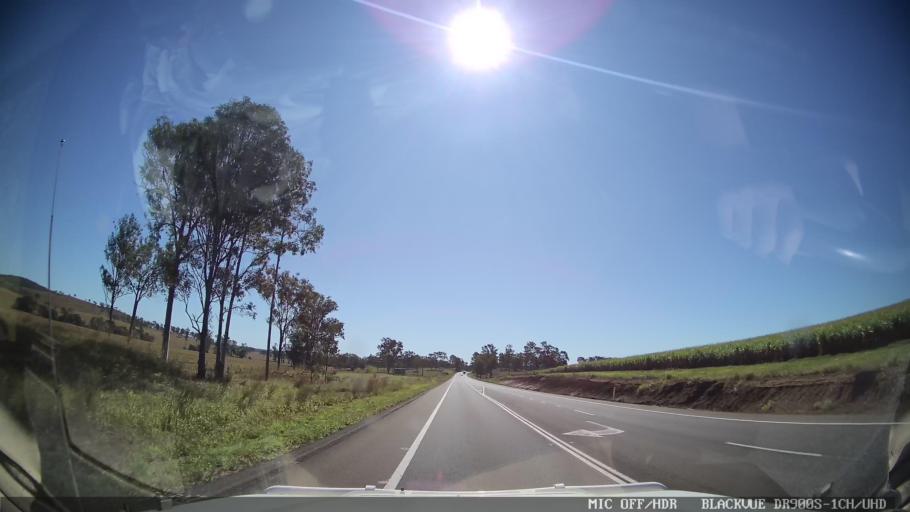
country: AU
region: Queensland
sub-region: Fraser Coast
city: Maryborough
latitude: -25.7788
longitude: 152.5962
